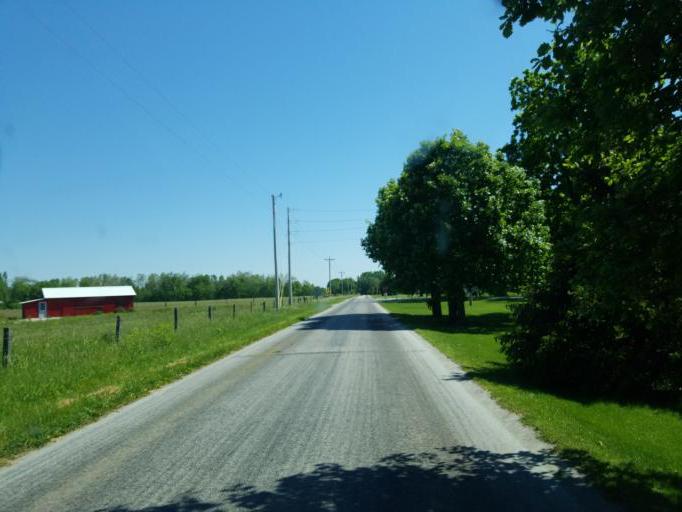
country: US
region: Ohio
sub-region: Hardin County
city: Kenton
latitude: 40.6156
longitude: -83.5035
